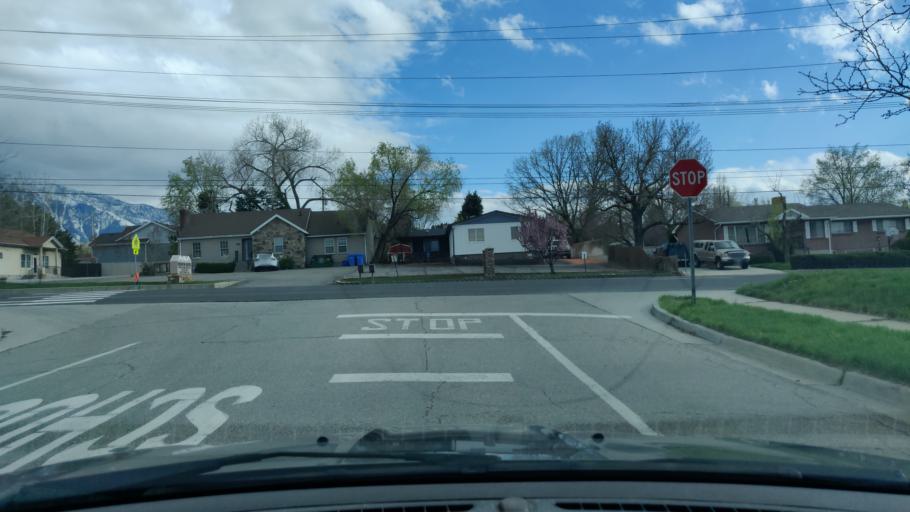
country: US
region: Utah
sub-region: Salt Lake County
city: Little Cottonwood Creek Valley
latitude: 40.6243
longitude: -111.8309
